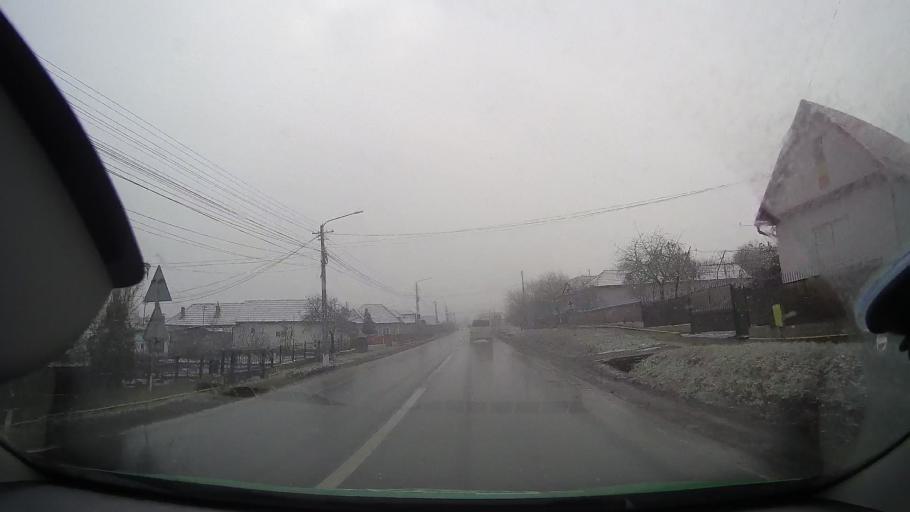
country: RO
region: Mures
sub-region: Comuna Bagaciu
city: Delenii
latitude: 46.2834
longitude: 24.3006
